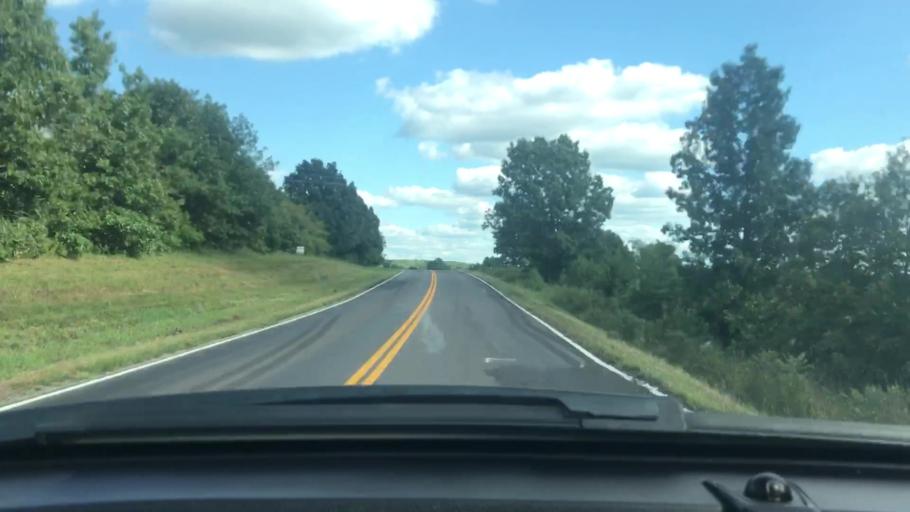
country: US
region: Missouri
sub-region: Wright County
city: Hartville
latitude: 37.3509
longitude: -92.3359
